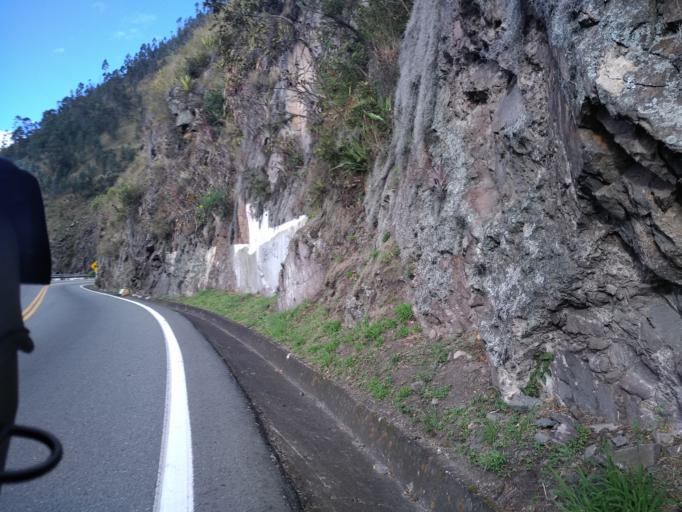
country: CO
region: Narino
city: Funes
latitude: 0.9497
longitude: -77.4727
